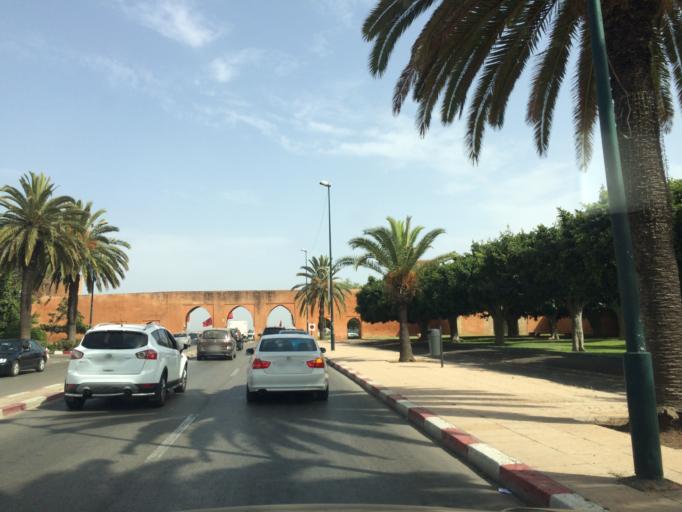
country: MA
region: Rabat-Sale-Zemmour-Zaer
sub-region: Rabat
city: Rabat
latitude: 34.0069
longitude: -6.8273
